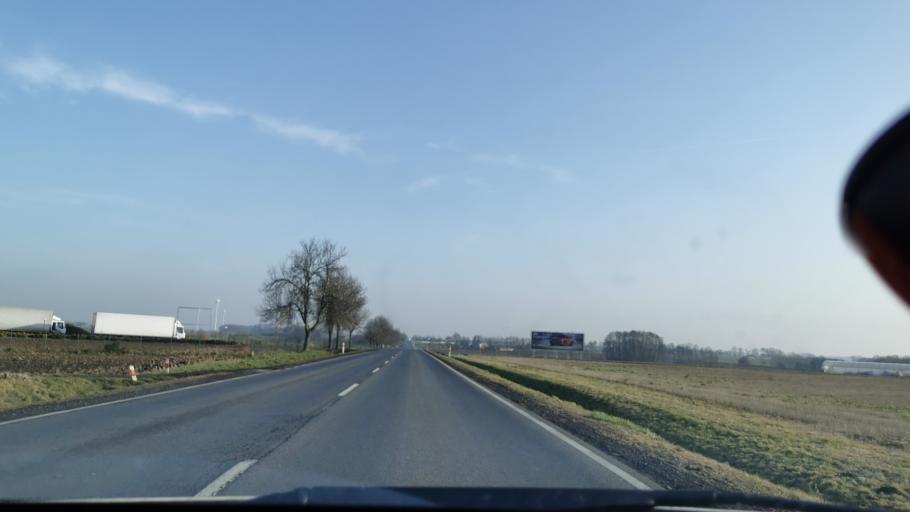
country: PL
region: Lodz Voivodeship
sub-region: Powiat sieradzki
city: Blaszki
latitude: 51.6799
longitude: 18.3452
